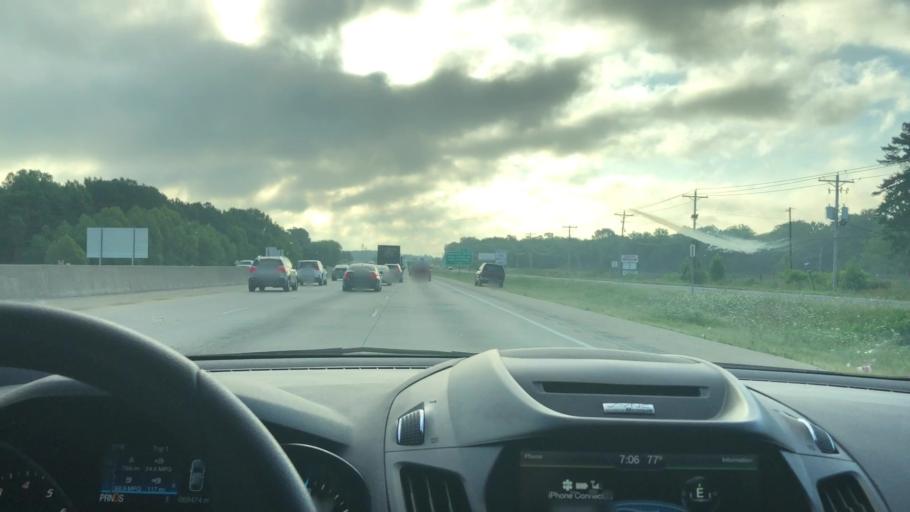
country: US
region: Arkansas
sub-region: Pulaski County
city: Alexander
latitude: 34.6457
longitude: -92.4308
